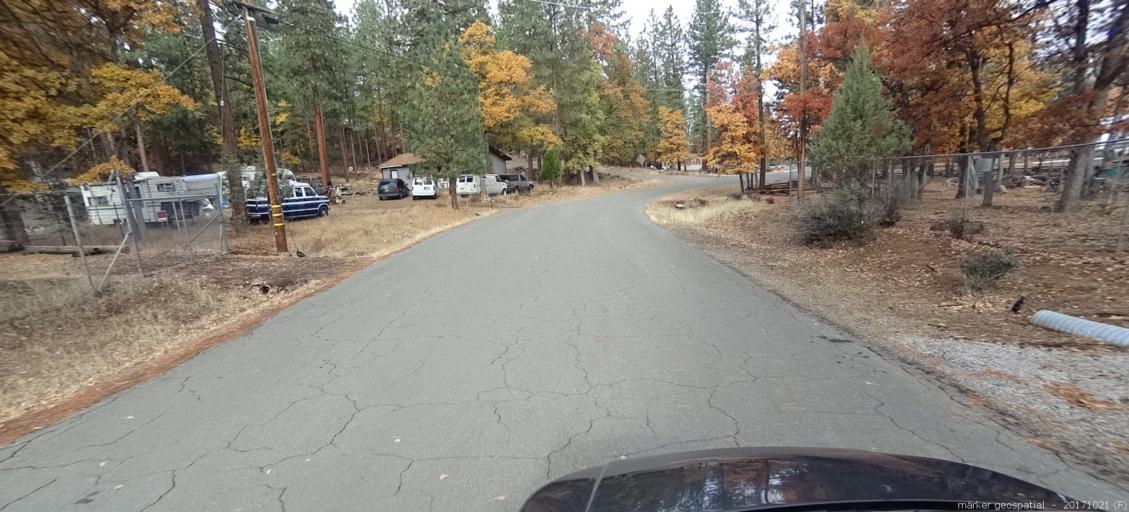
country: US
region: California
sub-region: Shasta County
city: Burney
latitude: 40.9144
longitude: -121.5580
